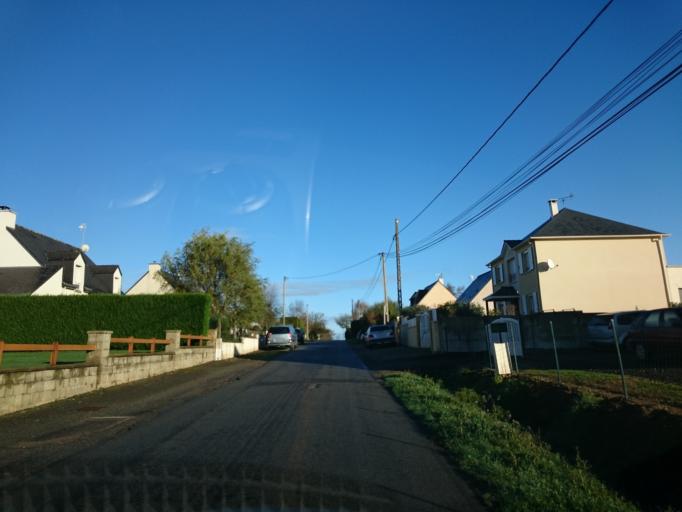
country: FR
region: Brittany
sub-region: Departement d'Ille-et-Vilaine
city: Chanteloup
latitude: 47.9233
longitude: -1.5875
